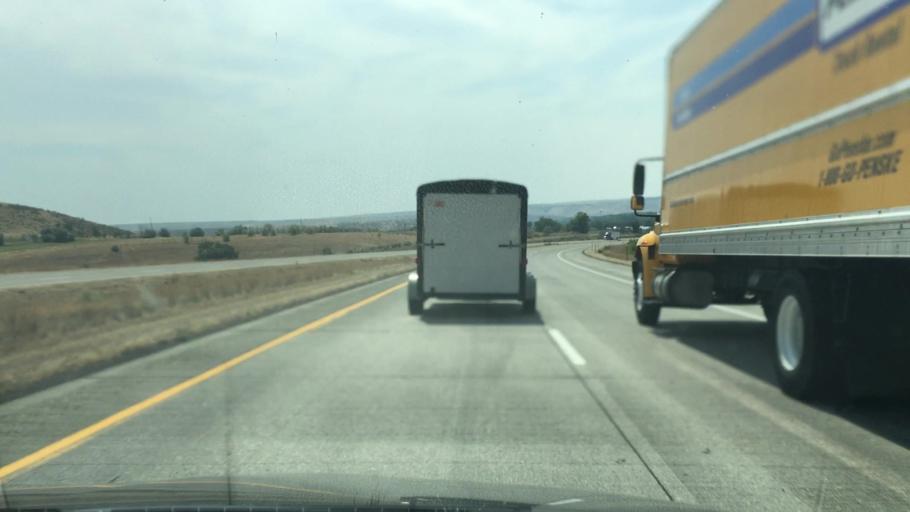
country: US
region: Idaho
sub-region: Elmore County
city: Glenns Ferry
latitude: 42.9635
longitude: -115.2573
